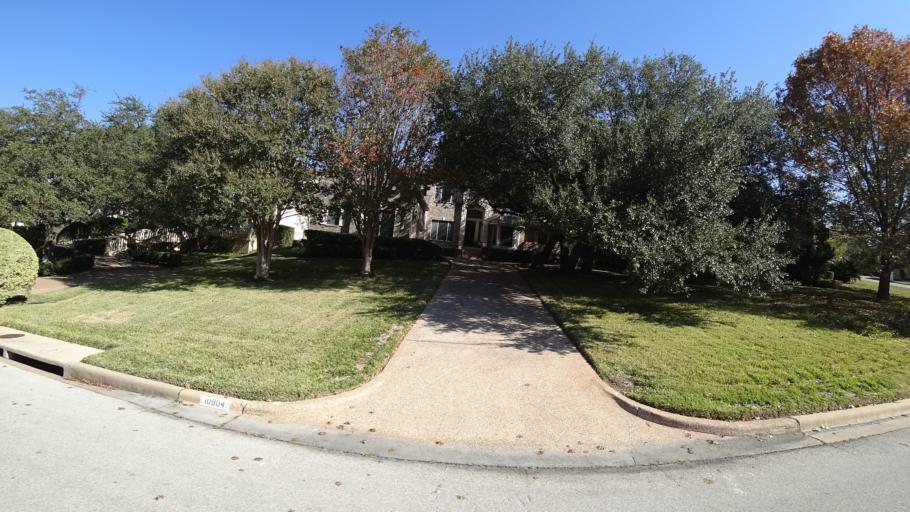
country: US
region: Texas
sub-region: Travis County
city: Lost Creek
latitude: 30.3716
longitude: -97.8637
